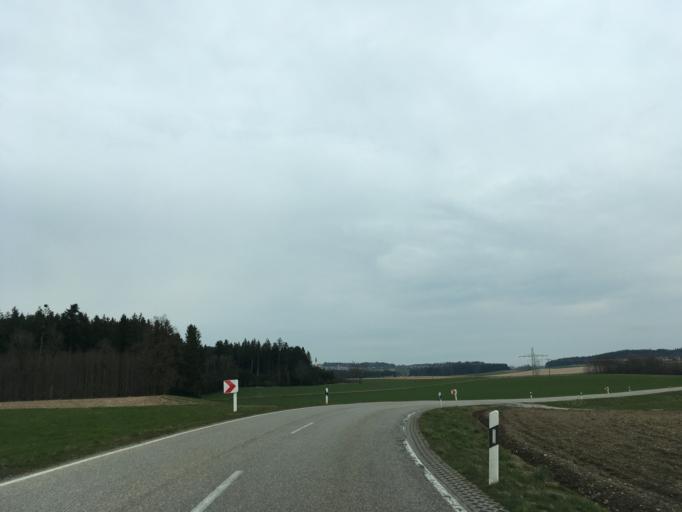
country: DE
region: Bavaria
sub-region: Upper Bavaria
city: Schnaitsee
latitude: 48.0421
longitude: 12.3703
